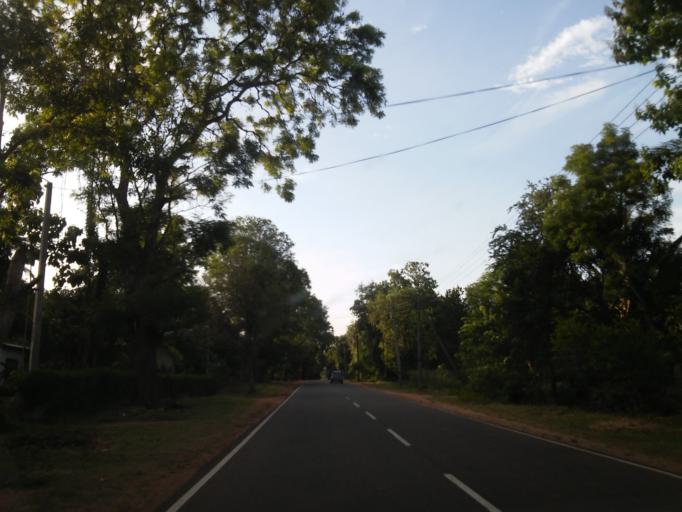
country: LK
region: Central
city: Sigiriya
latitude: 8.1068
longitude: 80.5889
